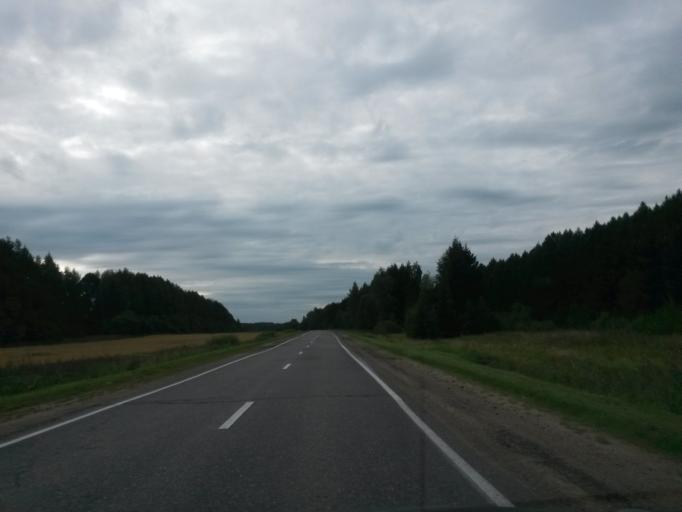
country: RU
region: Jaroslavl
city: Krasnyye Tkachi
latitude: 57.3918
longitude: 39.6825
